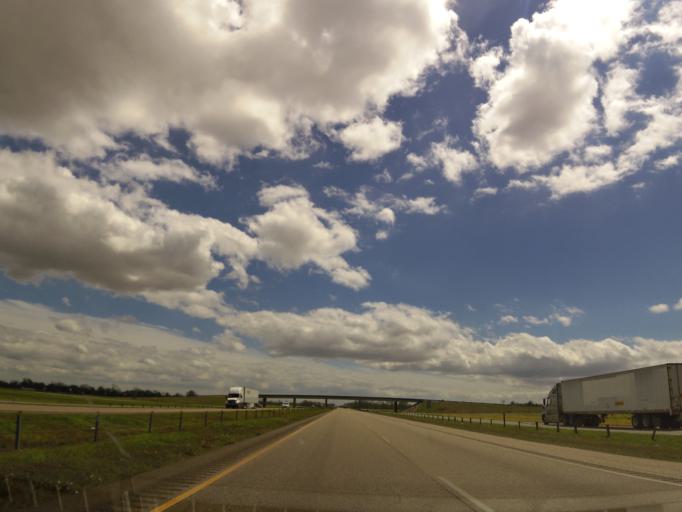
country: US
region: Arkansas
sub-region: Crittenden County
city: Marion
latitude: 35.2948
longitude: -90.2452
